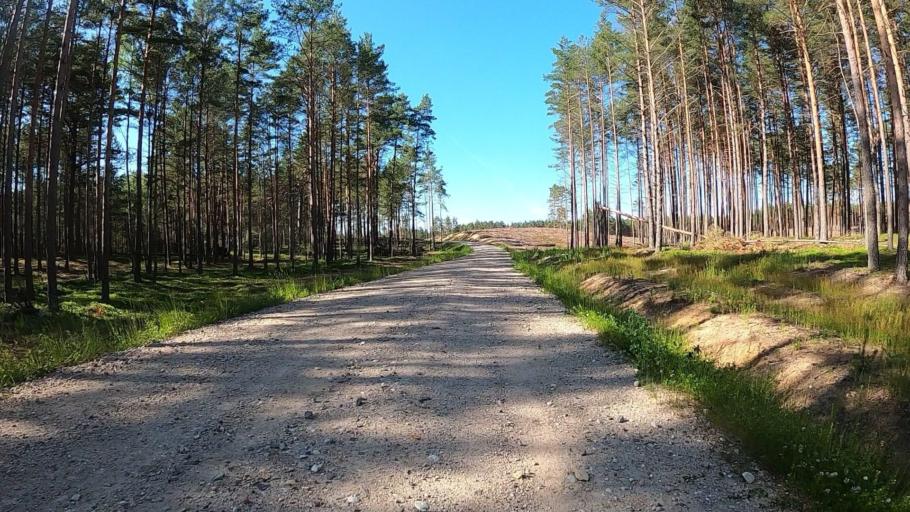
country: LV
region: Carnikava
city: Carnikava
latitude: 57.0914
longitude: 24.2471
